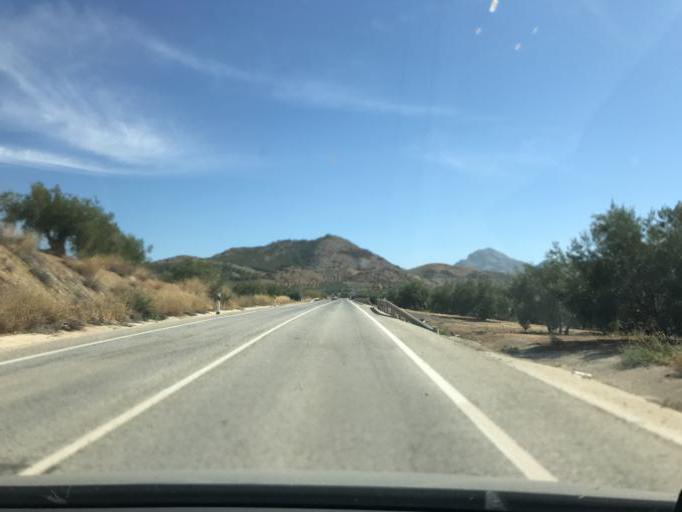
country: ES
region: Andalusia
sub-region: Provincia de Jaen
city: Alcaudete
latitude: 37.5851
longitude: -4.1387
